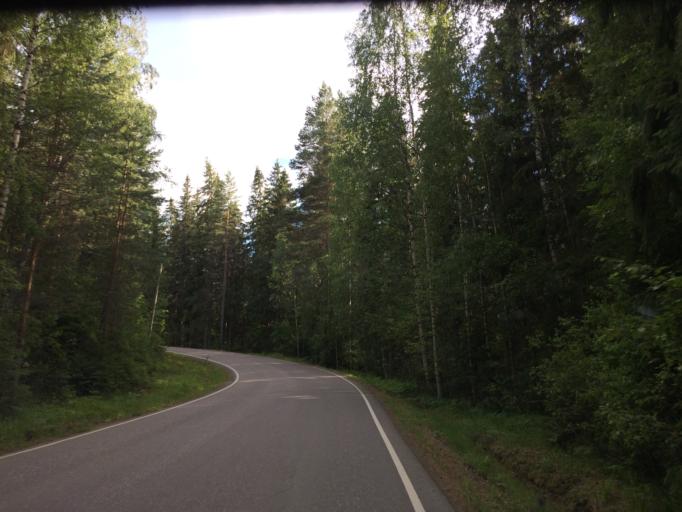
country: FI
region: Haeme
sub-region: Haemeenlinna
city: Janakkala
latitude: 60.8638
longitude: 24.5503
